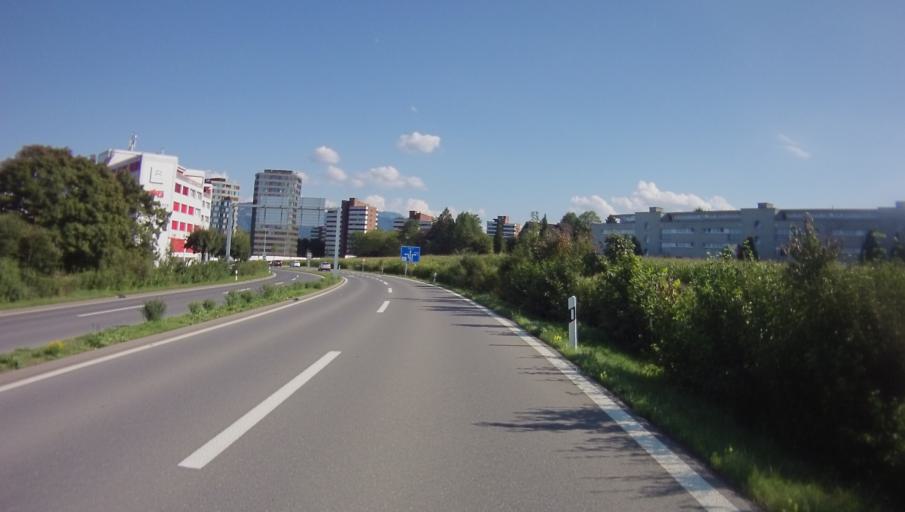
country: CH
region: Zug
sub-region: Zug
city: Cham
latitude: 47.1875
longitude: 8.4713
